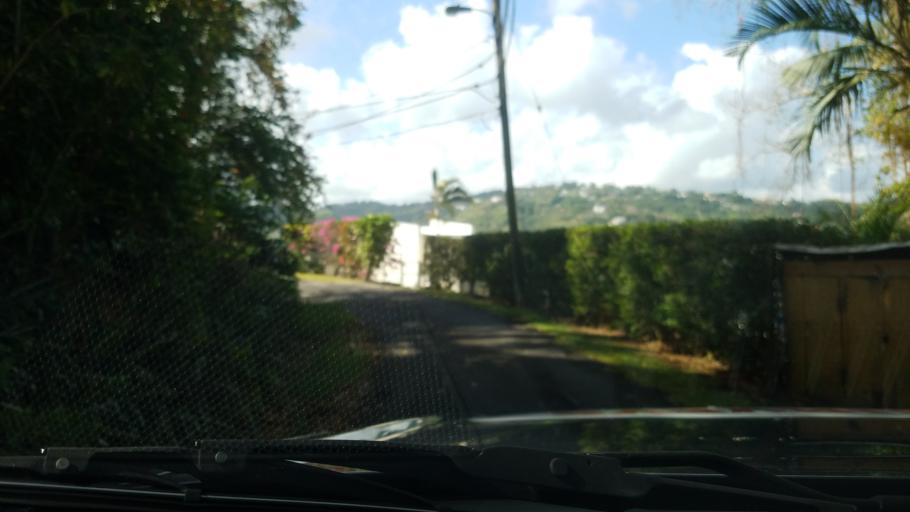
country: LC
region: Castries Quarter
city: Bisee
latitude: 14.0207
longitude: -60.9995
